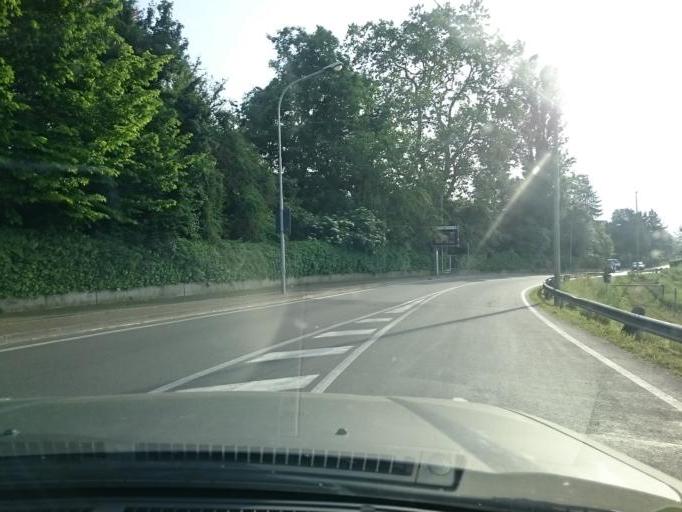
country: IT
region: Veneto
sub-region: Provincia di Padova
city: Noventa
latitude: 45.4068
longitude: 11.9484
